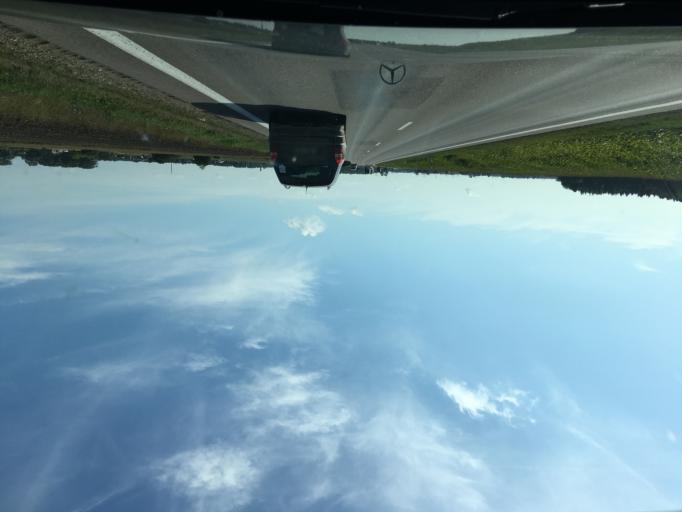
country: LT
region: Panevezys
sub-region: Panevezys City
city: Panevezys
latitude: 55.7919
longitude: 24.3140
